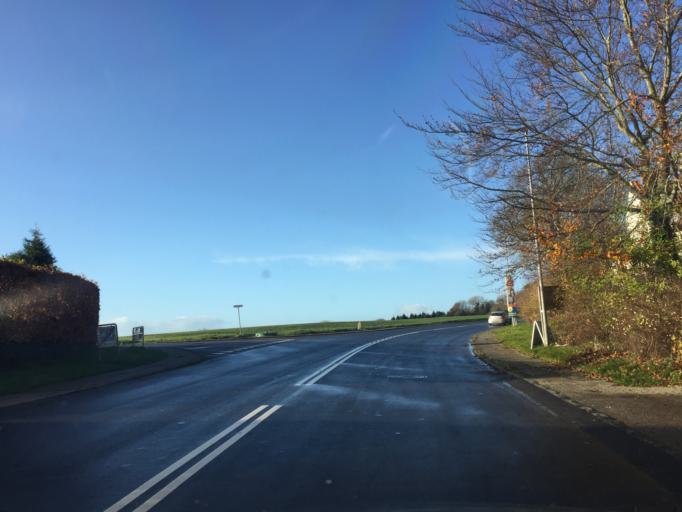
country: DK
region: South Denmark
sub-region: Kolding Kommune
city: Sonder Bjert
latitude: 55.4610
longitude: 9.6113
